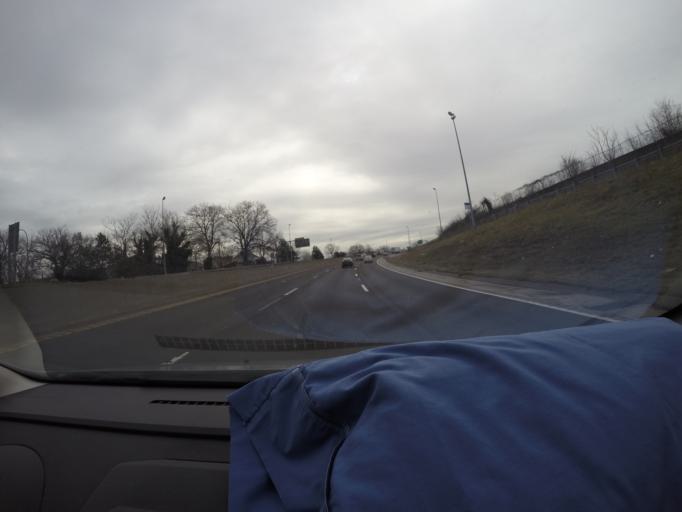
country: US
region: Missouri
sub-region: Saint Louis County
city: Pine Lawn
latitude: 38.7003
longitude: -90.2635
